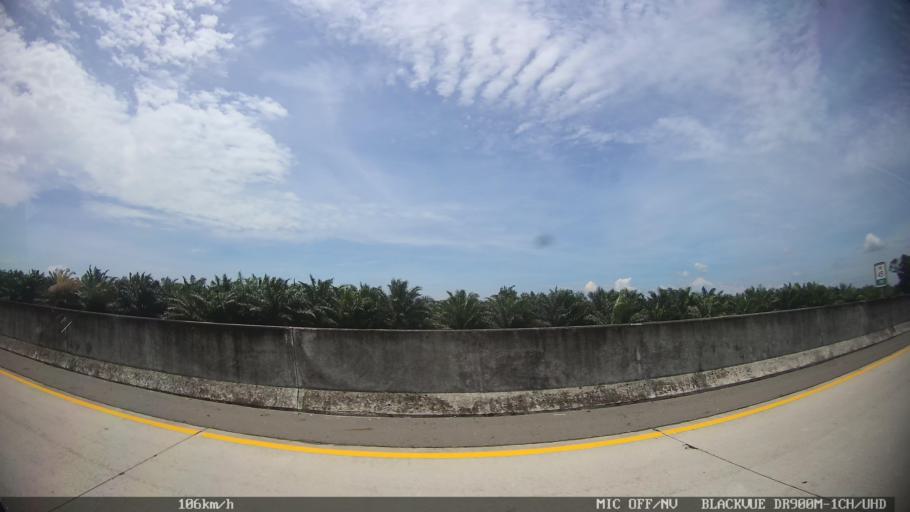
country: ID
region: North Sumatra
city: Perbaungan
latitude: 3.5320
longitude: 98.8756
